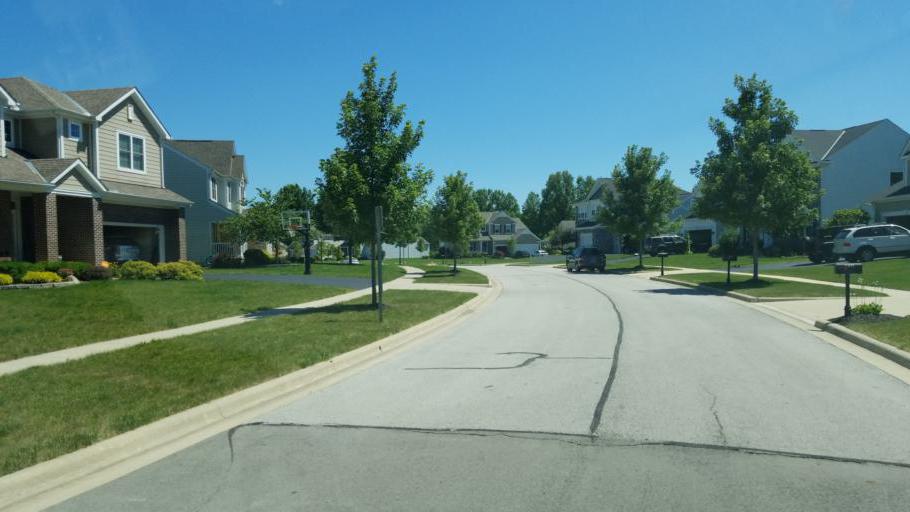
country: US
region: Ohio
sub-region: Franklin County
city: Westerville
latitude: 40.1855
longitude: -82.9073
